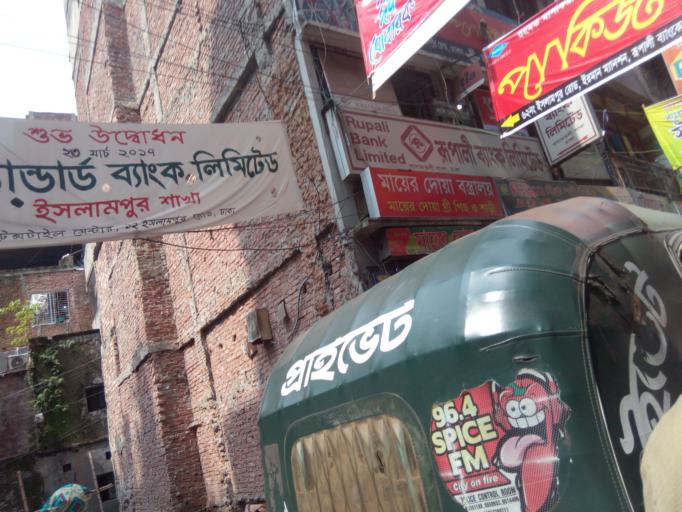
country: BD
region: Dhaka
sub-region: Dhaka
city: Dhaka
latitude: 23.7119
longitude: 90.4039
